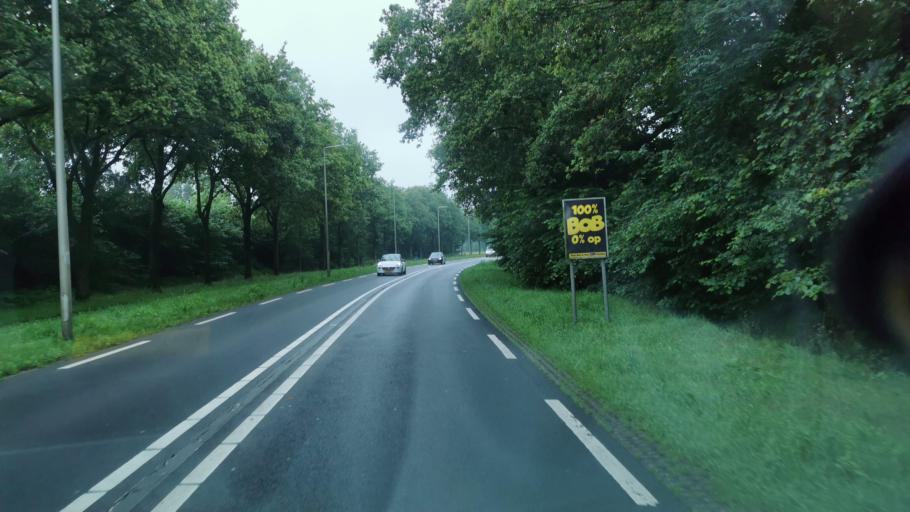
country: NL
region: Overijssel
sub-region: Gemeente Losser
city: Losser
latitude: 52.2515
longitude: 7.0128
